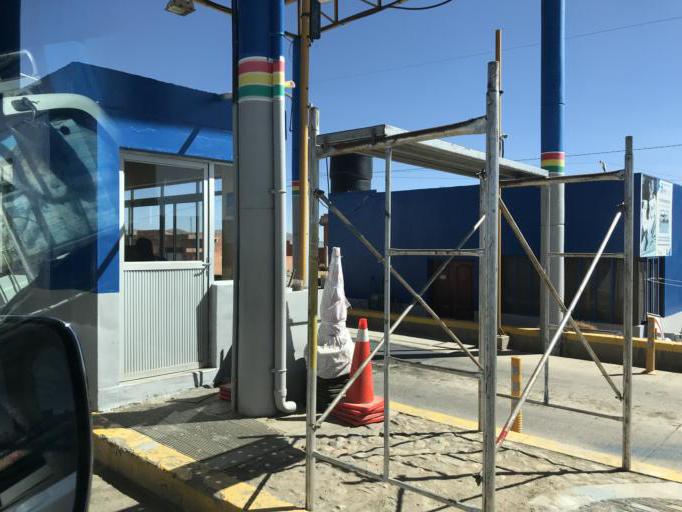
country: BO
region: La Paz
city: La Paz
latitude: -16.5312
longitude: -68.3865
